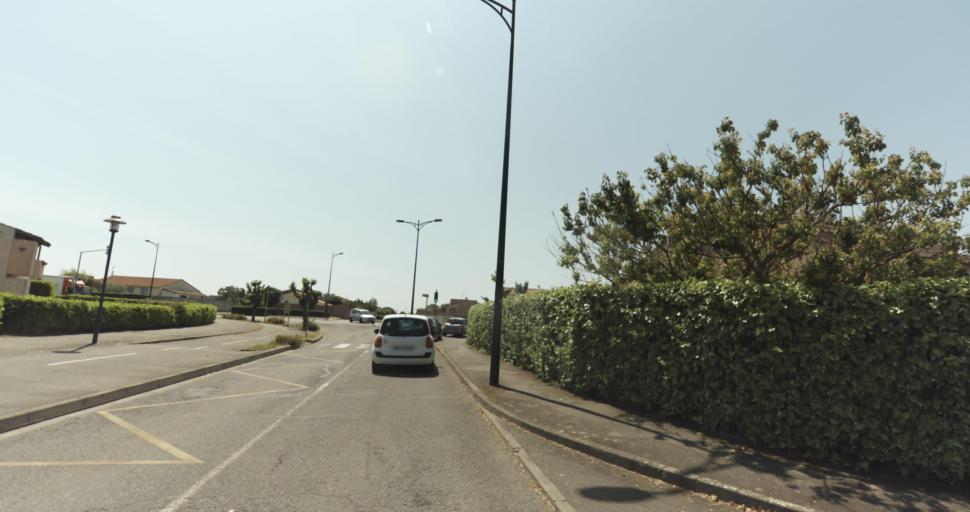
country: FR
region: Midi-Pyrenees
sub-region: Departement de la Haute-Garonne
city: Plaisance-du-Touch
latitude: 43.5615
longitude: 1.3050
